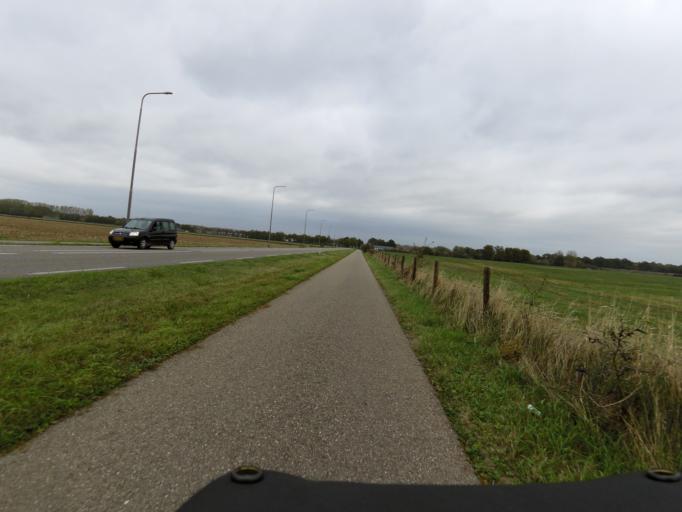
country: NL
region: Gelderland
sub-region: Gemeente Zevenaar
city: Zevenaar
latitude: 51.9001
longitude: 6.1084
